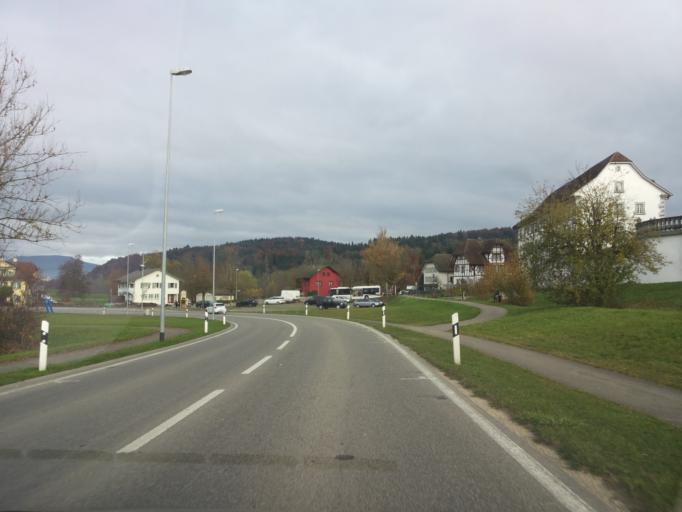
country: CH
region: Bern
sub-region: Oberaargau
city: Roggwil
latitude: 47.2311
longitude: 7.8387
